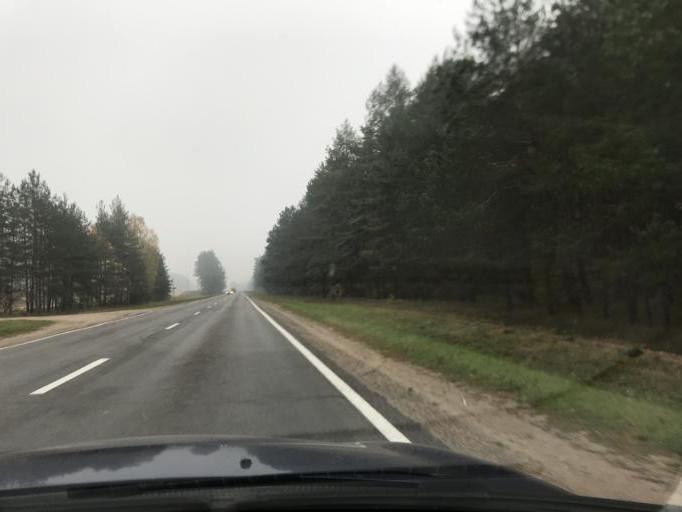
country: BY
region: Grodnenskaya
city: Hrodna
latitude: 53.7926
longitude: 23.8547
